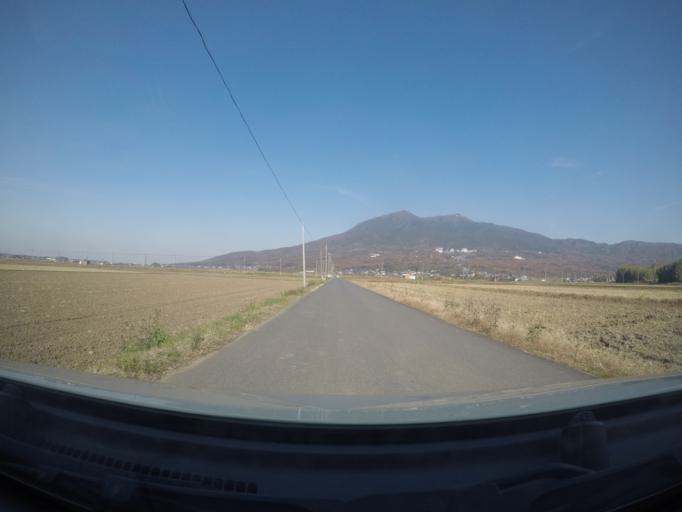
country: JP
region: Ibaraki
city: Tsukuba
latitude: 36.1928
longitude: 140.0895
